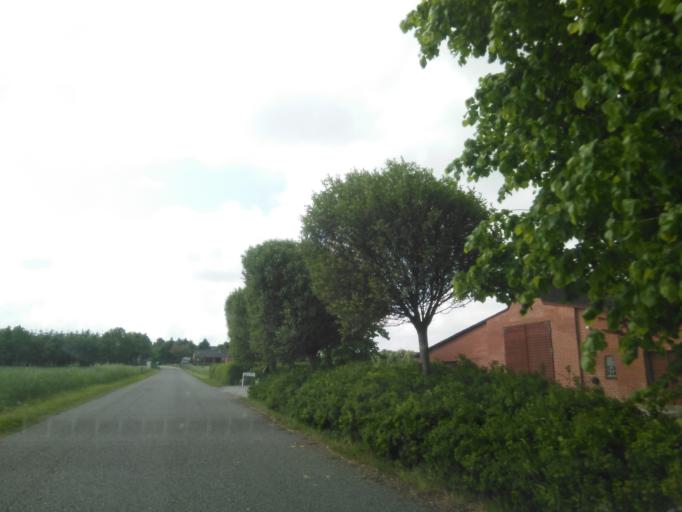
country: DK
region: Central Jutland
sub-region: Skanderborg Kommune
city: Skovby
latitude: 56.2039
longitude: 9.9684
